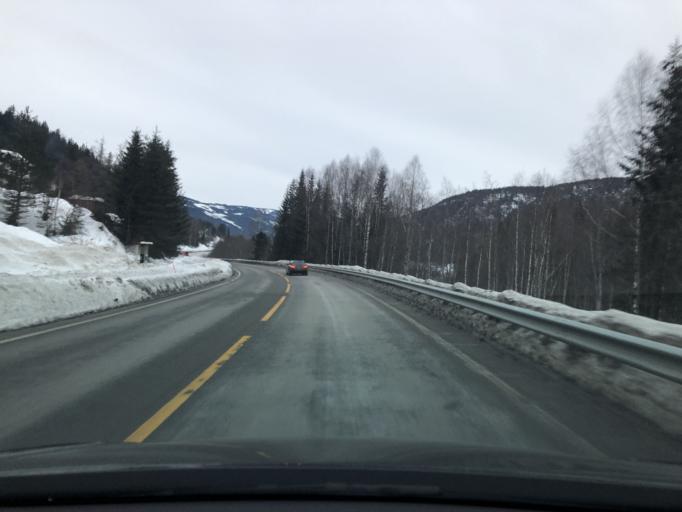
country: NO
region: Oppland
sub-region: Nordre Land
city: Dokka
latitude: 60.6519
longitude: 9.8354
